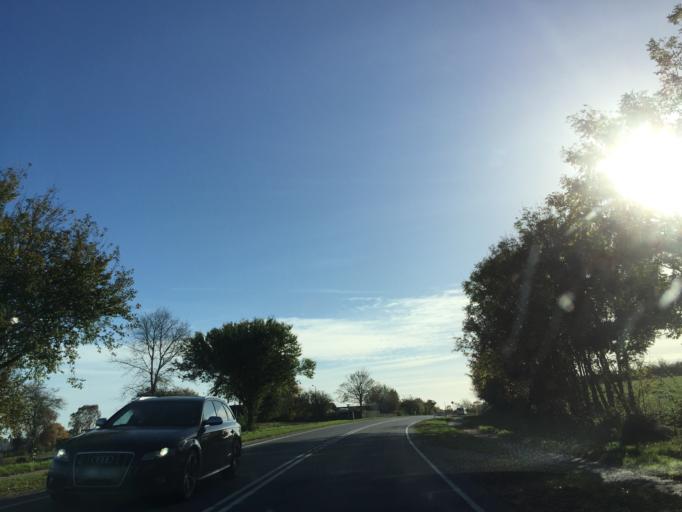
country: DK
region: South Denmark
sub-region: Sonderborg Kommune
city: Dybbol
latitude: 54.9193
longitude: 9.7564
